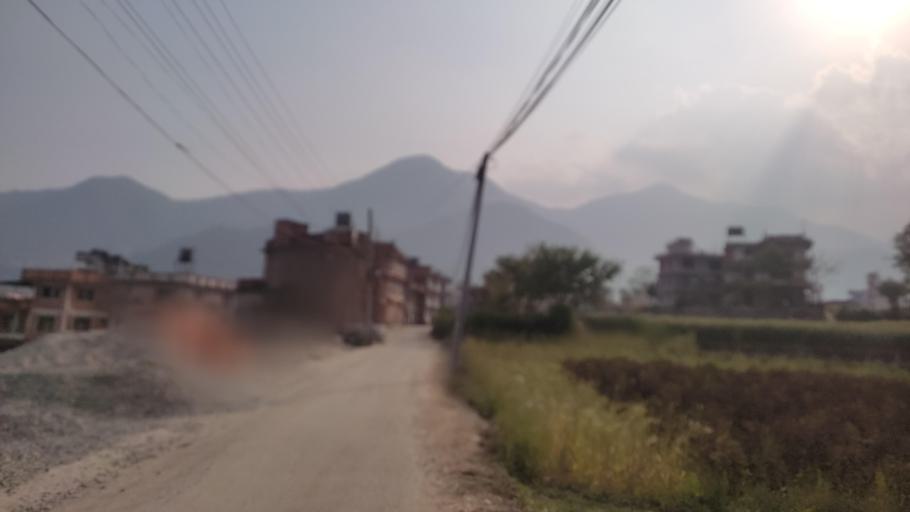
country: NP
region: Central Region
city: Kirtipur
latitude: 27.6674
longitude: 85.2785
